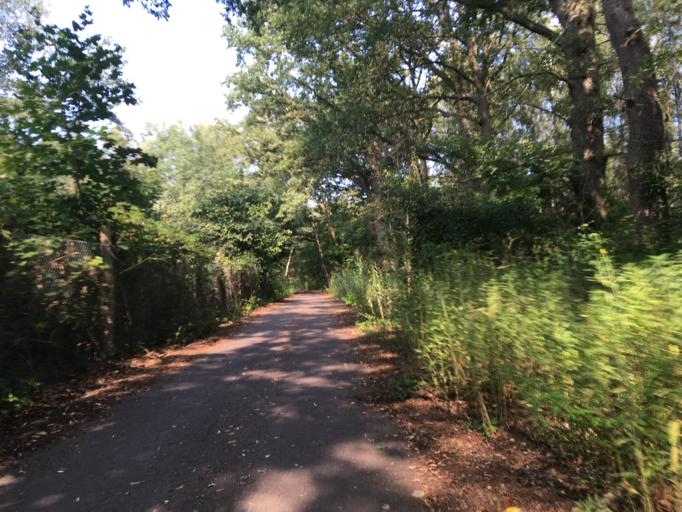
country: DE
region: Berlin
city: Falkenhagener Feld
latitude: 52.5980
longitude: 13.1647
